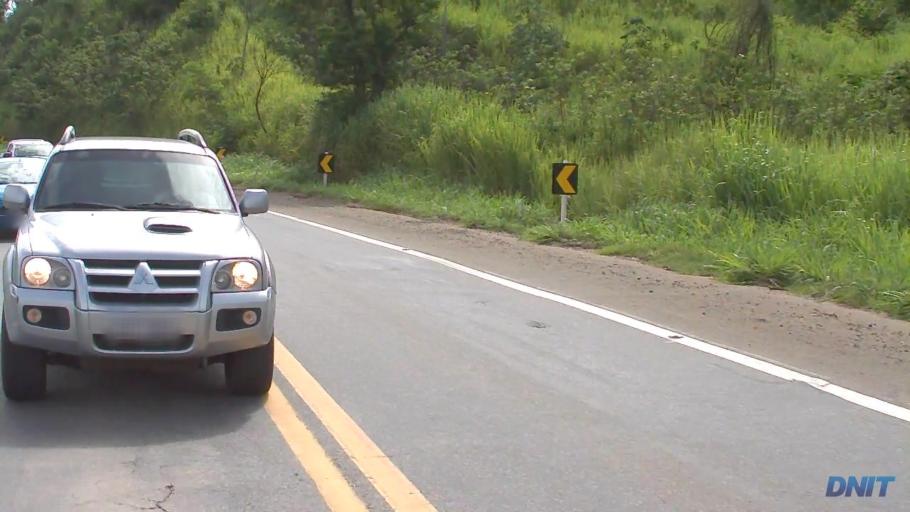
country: BR
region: Minas Gerais
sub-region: Ipaba
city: Ipaba
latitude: -19.3680
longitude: -42.4514
